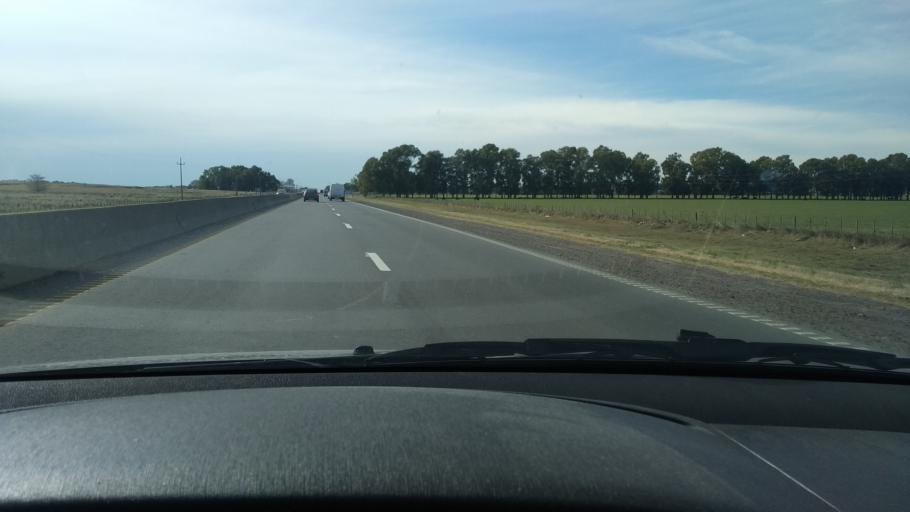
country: AR
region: Buenos Aires
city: Olavarria
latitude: -36.9222
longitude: -60.2117
